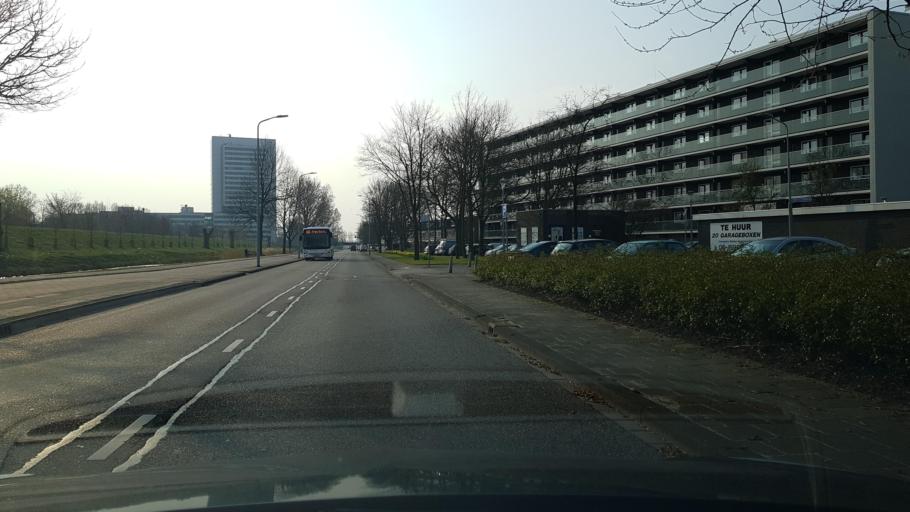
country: NL
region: North Holland
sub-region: Gemeente Haarlemmermeer
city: Hoofddorp
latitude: 52.2966
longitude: 4.6916
